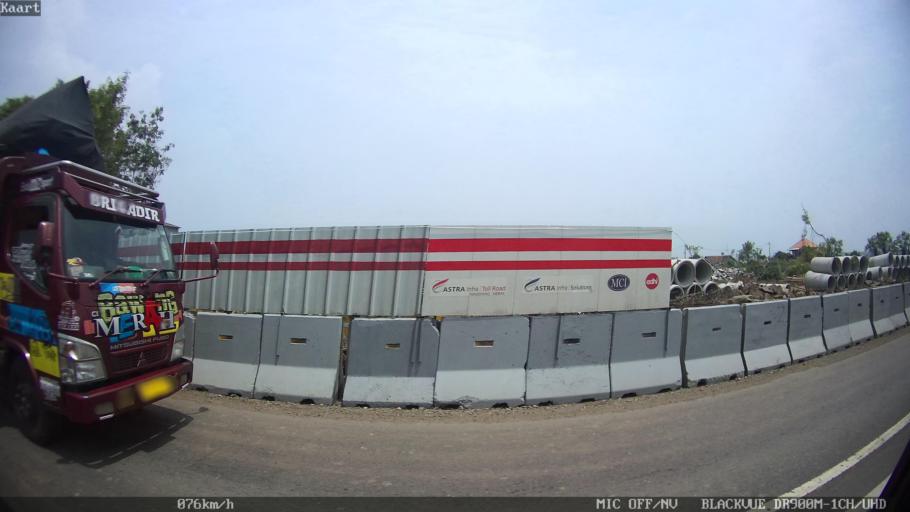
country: ID
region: West Java
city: Kresek
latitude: -6.1497
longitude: 106.3053
